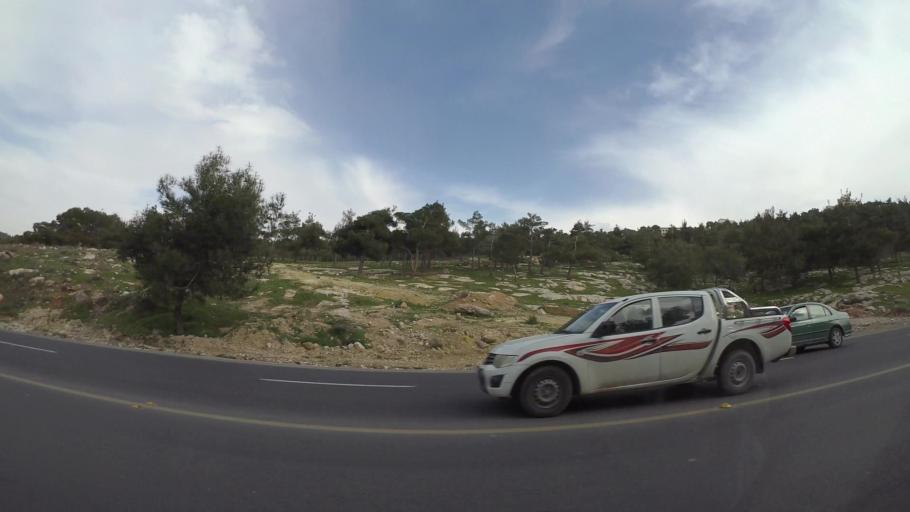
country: JO
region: Amman
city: Amman
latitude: 32.0159
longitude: 35.9352
